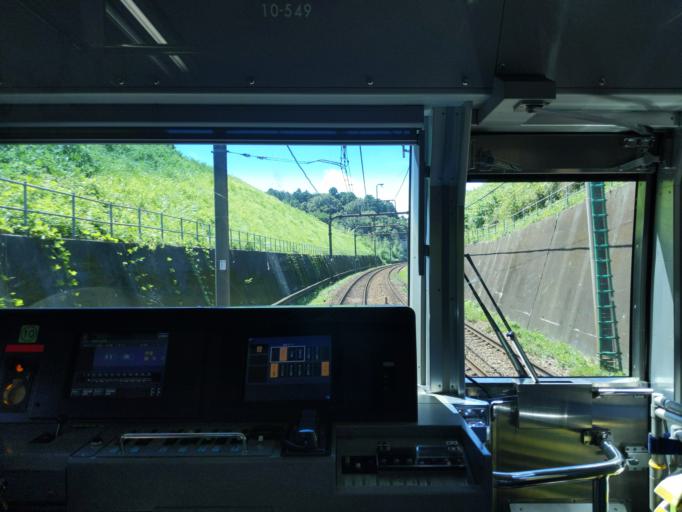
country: JP
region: Tokyo
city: Chofugaoka
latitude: 35.6213
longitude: 139.4834
